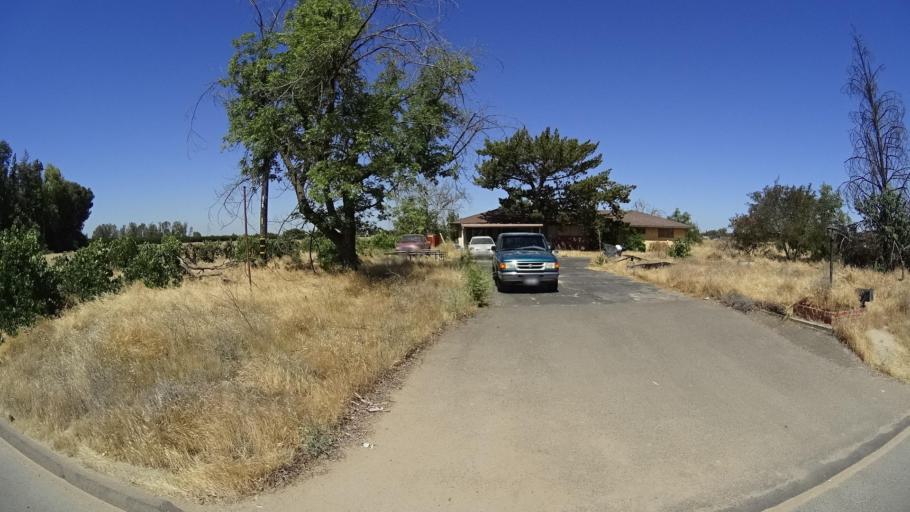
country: US
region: California
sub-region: Fresno County
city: Sunnyside
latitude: 36.7200
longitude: -119.6731
